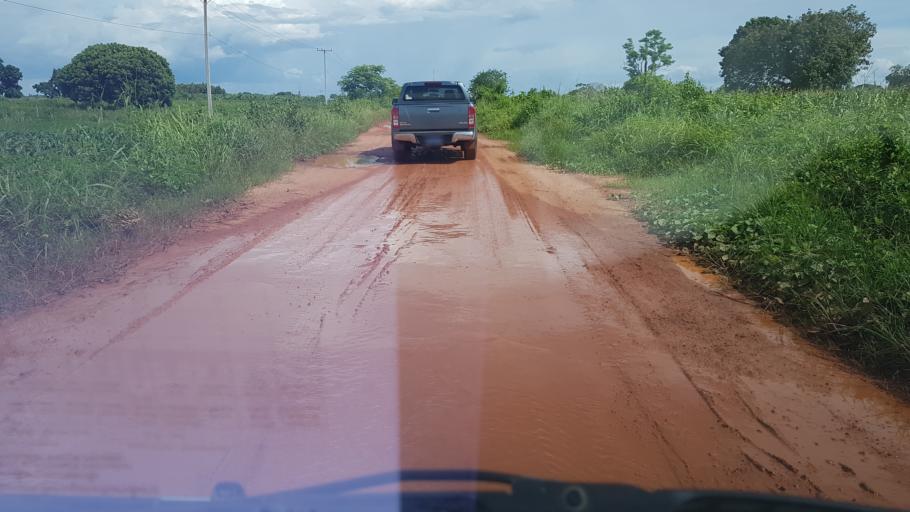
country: LA
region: Vientiane
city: Vientiane
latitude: 18.2298
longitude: 102.5640
